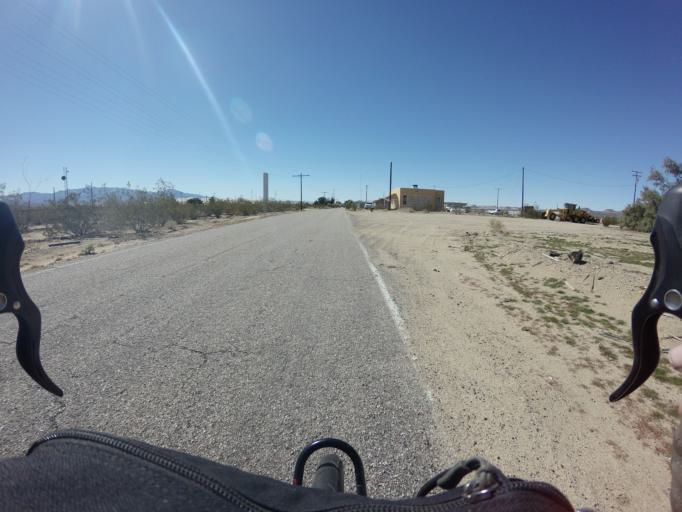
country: US
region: Nevada
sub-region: Clark County
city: Sandy Valley
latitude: 35.0150
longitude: -115.6482
